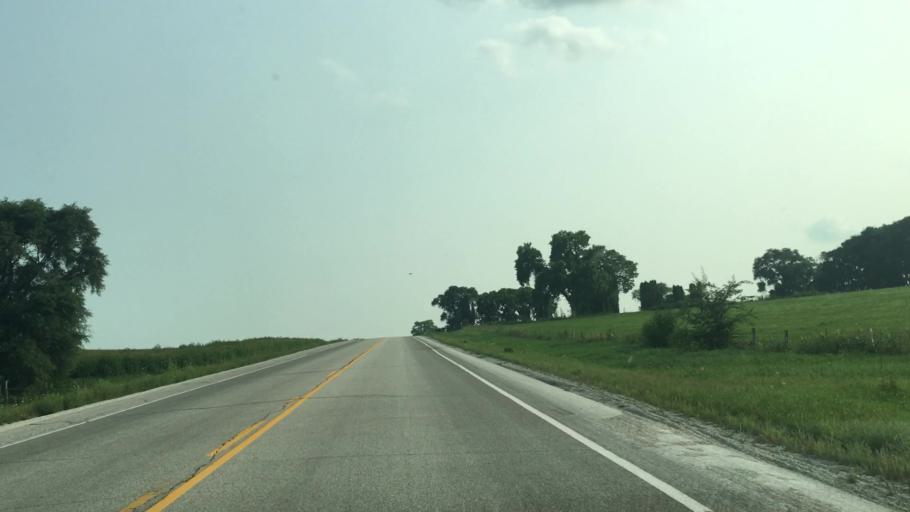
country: US
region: Minnesota
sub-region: Fillmore County
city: Harmony
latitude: 43.5419
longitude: -91.9296
